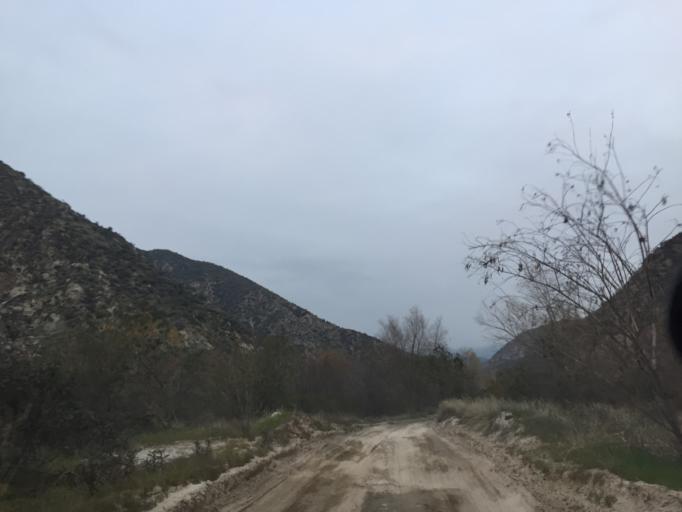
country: US
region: California
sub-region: San Bernardino County
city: Mentone
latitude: 34.1228
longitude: -117.0793
